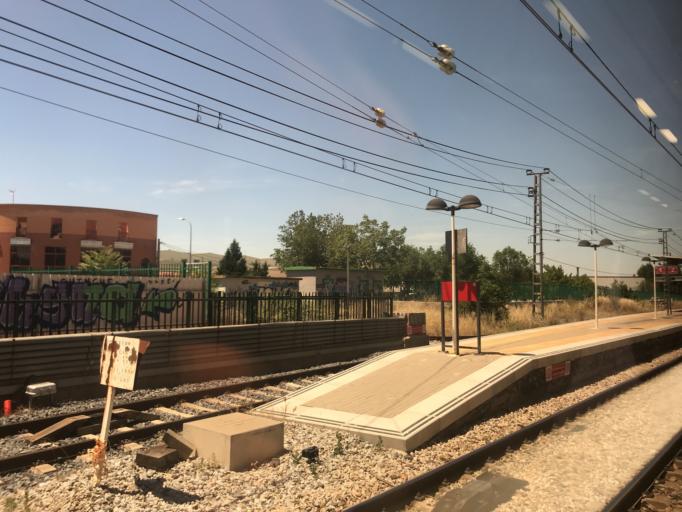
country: ES
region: Madrid
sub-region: Provincia de Madrid
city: Pinto
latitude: 40.2423
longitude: -3.7039
